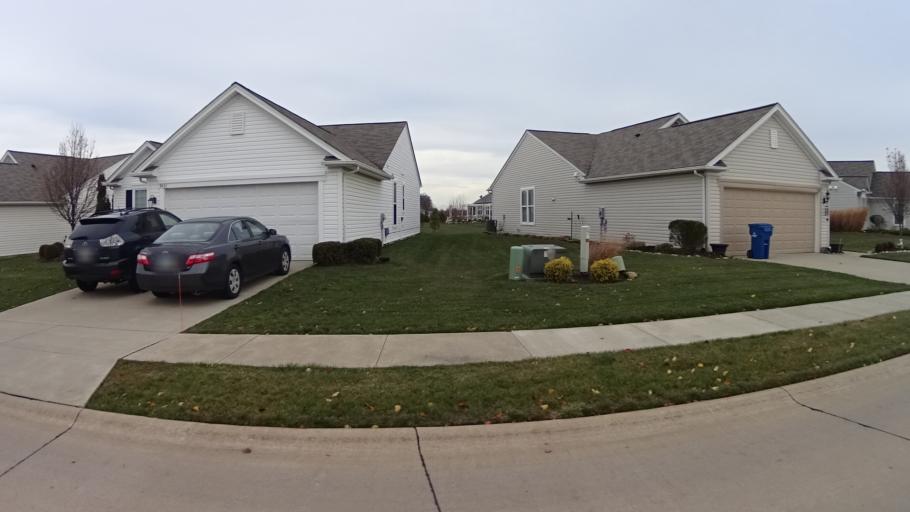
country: US
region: Ohio
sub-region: Lorain County
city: North Ridgeville
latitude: 41.3522
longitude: -82.0500
